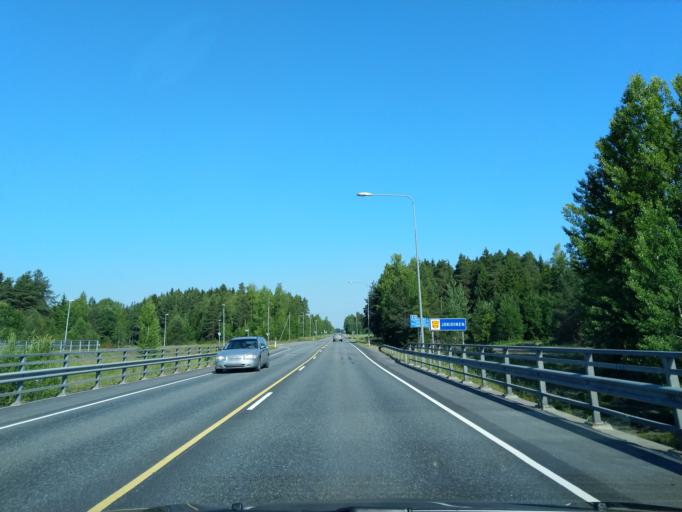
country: FI
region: Haeme
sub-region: Forssa
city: Forssa
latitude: 60.8307
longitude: 23.5624
